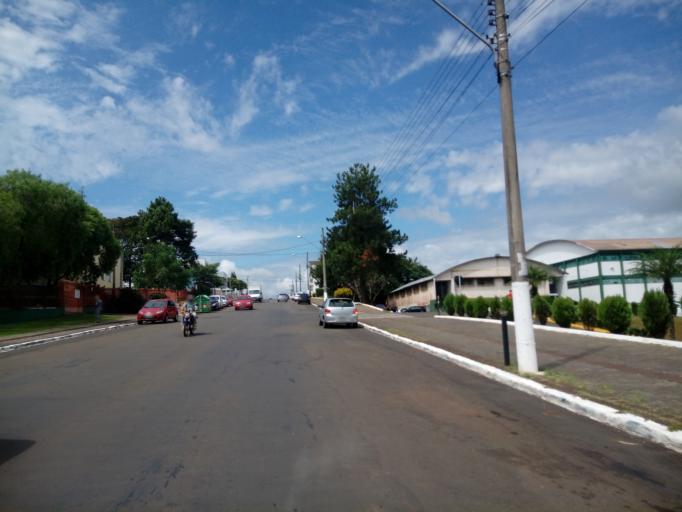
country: BR
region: Santa Catarina
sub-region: Chapeco
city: Chapeco
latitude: -27.1032
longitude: -52.6051
